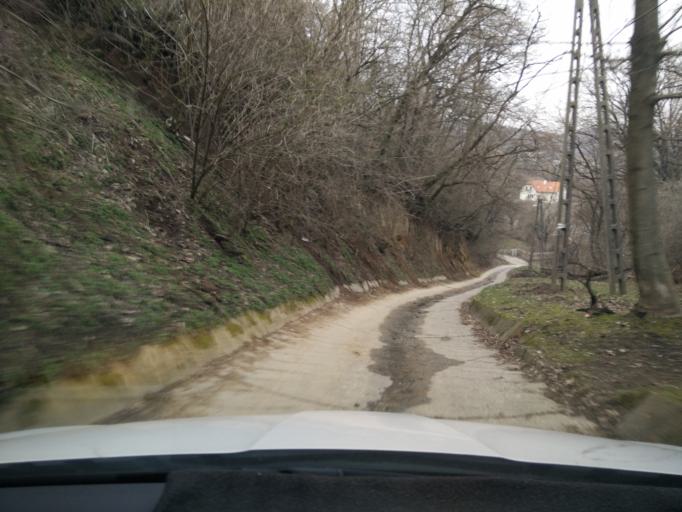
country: HU
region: Tolna
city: Szekszard
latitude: 46.3492
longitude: 18.6749
